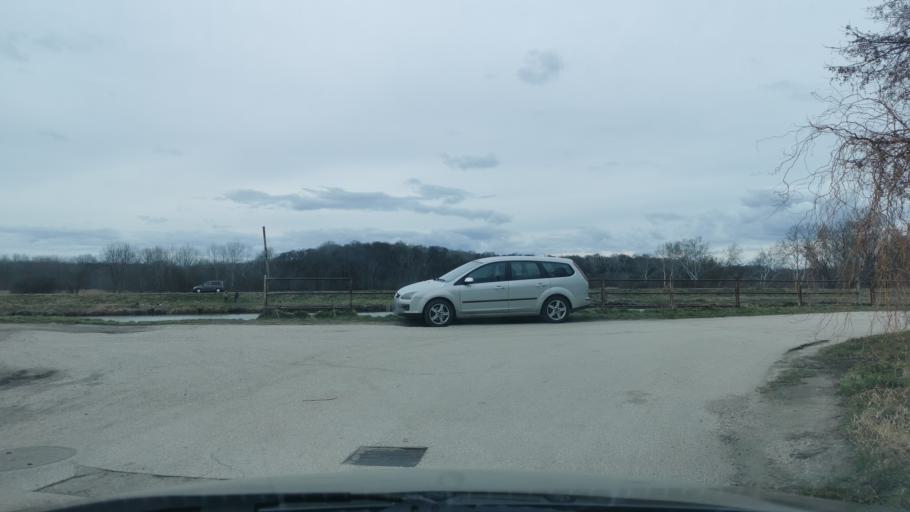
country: CZ
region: South Moravian
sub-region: Okres Breclav
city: Lanzhot
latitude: 48.6932
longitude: 17.0082
